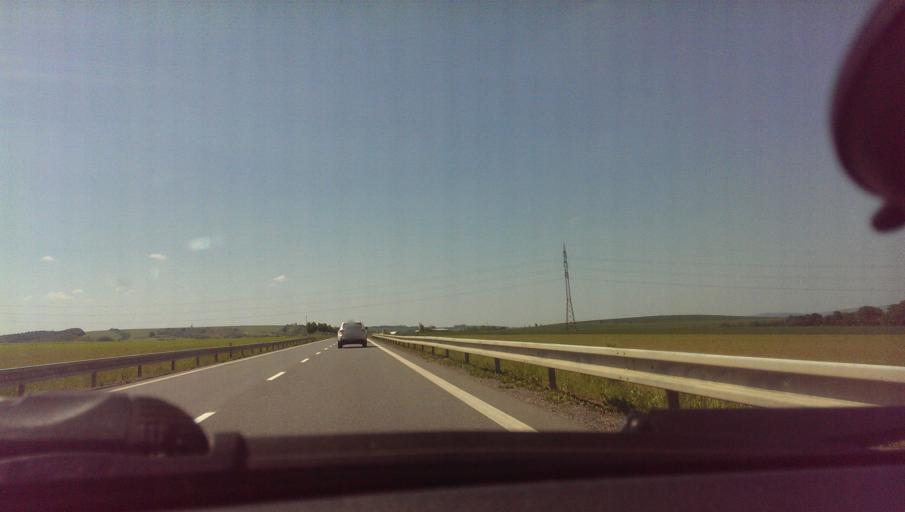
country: CZ
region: Zlin
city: Brezolupy
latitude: 49.1120
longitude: 17.5661
